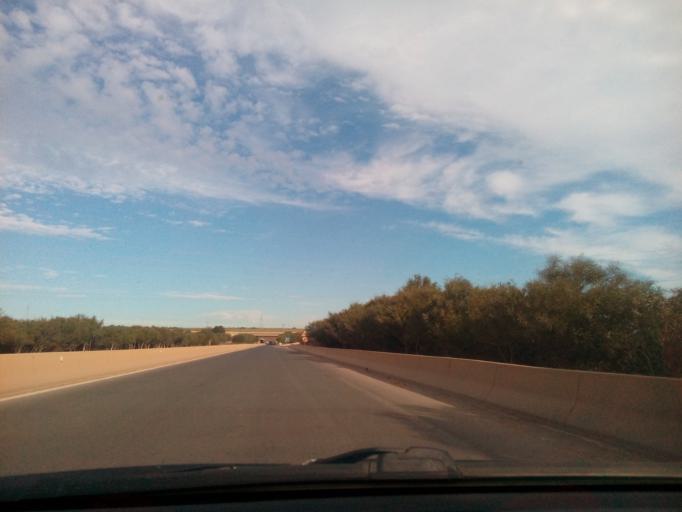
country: DZ
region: Mascara
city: Sig
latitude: 35.5403
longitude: -0.3782
